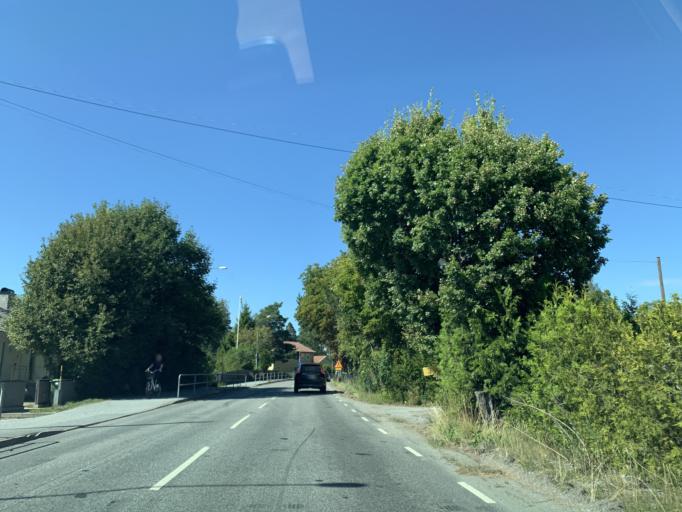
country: SE
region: Stockholm
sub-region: Ekero Kommun
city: Ekeroe
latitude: 59.2736
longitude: 17.7880
